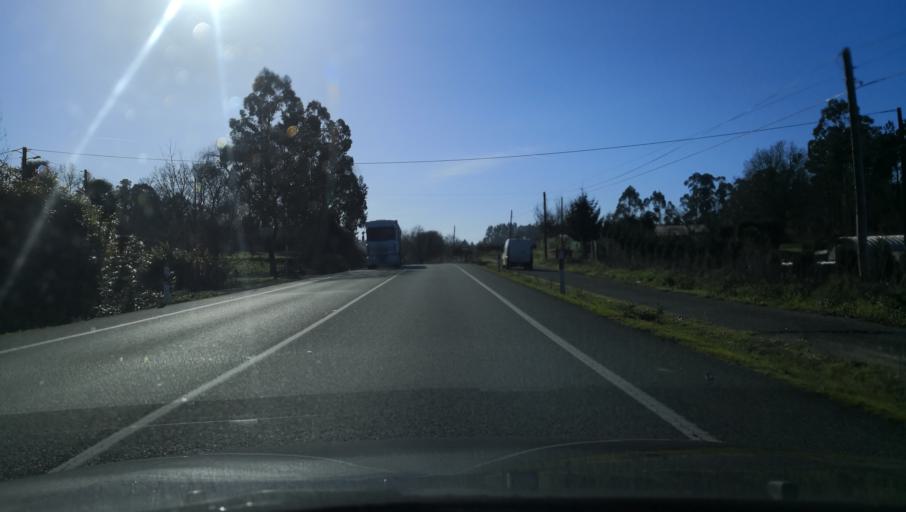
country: ES
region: Galicia
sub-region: Provincia da Coruna
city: Vedra
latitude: 42.8095
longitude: -8.4796
